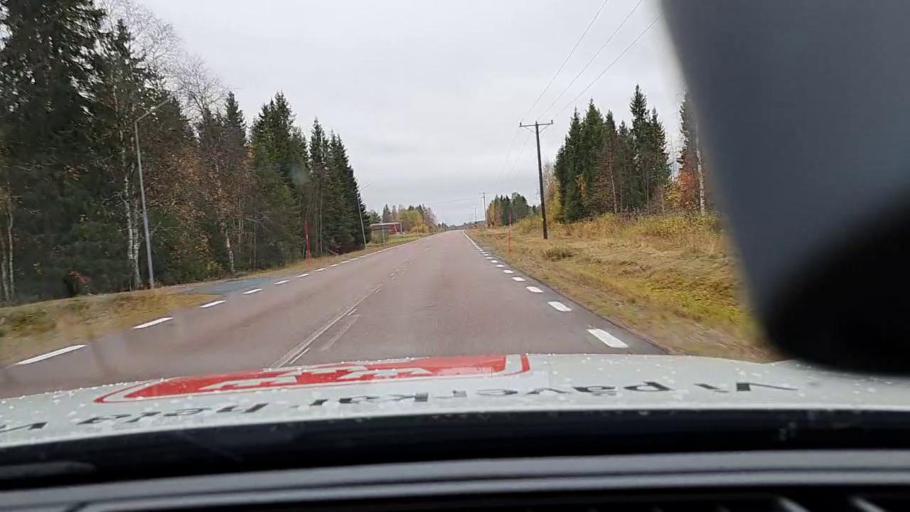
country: FI
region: Lapland
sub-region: Torniolaakso
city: Ylitornio
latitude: 66.1438
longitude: 23.8970
